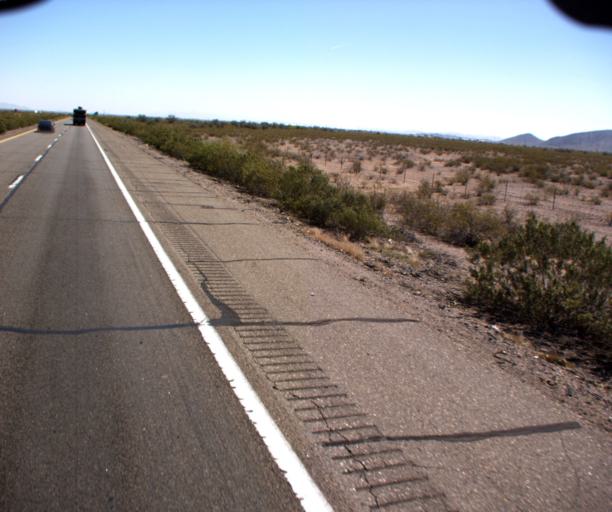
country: US
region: Arizona
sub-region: Maricopa County
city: Buckeye
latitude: 33.5051
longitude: -112.9801
